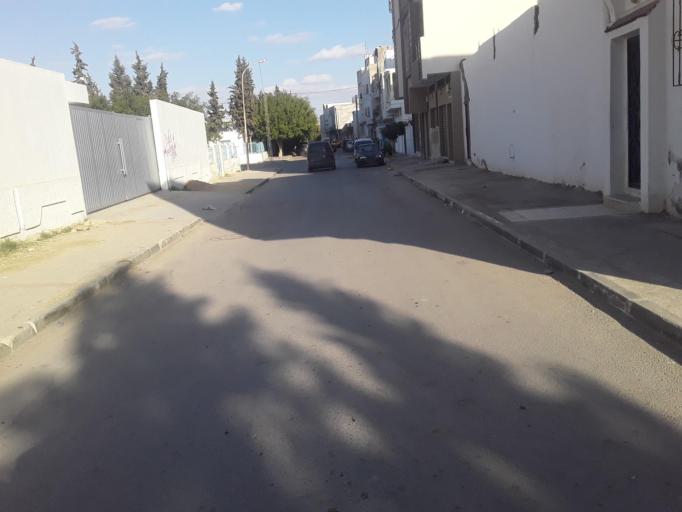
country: TN
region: Al Qayrawan
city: Kairouan
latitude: 35.6807
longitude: 10.0994
